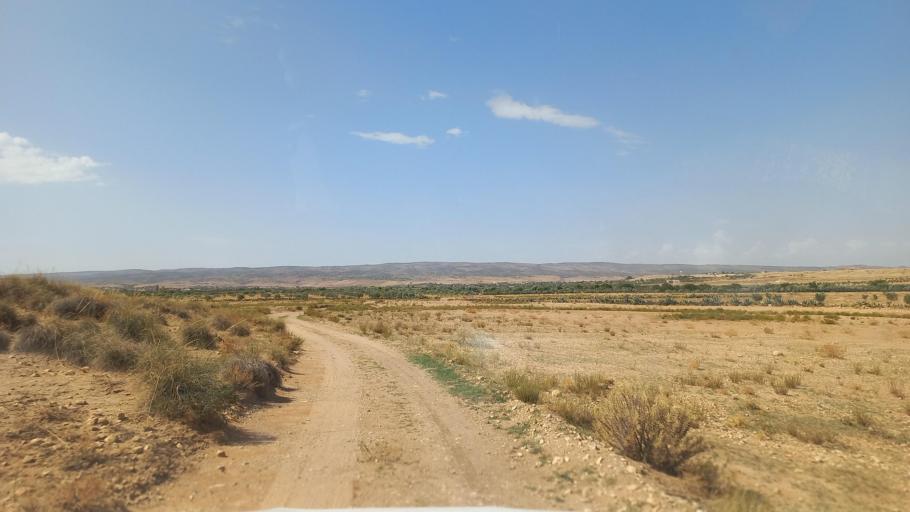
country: TN
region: Al Qasrayn
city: Kasserine
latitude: 35.2555
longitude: 8.9560
